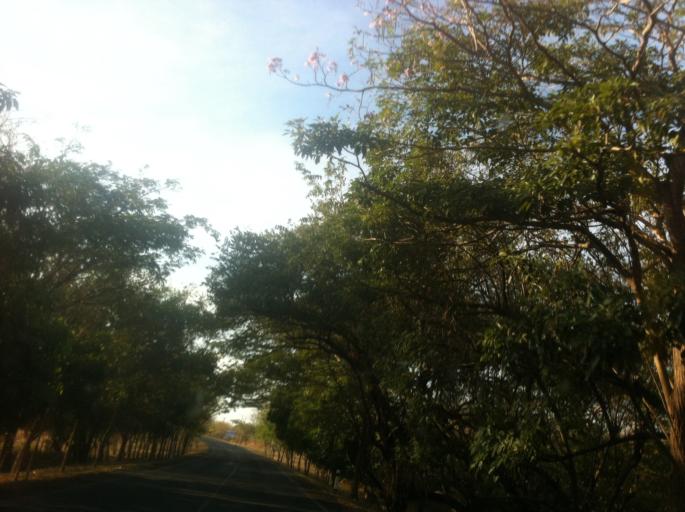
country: NI
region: Rivas
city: San Jorge
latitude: 11.3112
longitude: -85.7005
